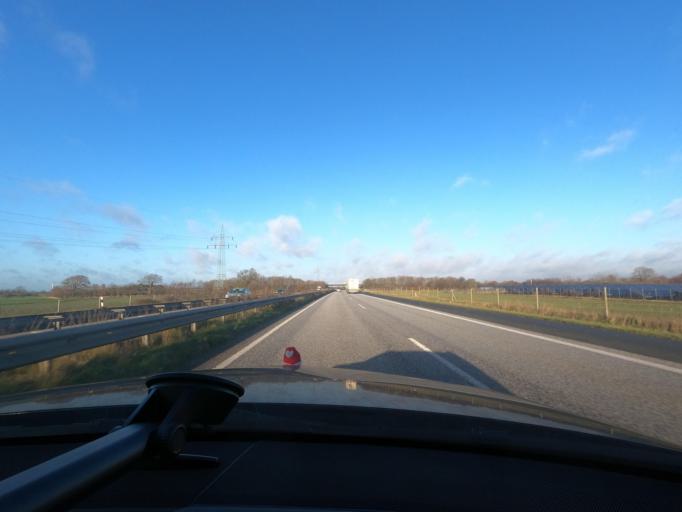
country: DE
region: Schleswig-Holstein
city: Lurschau
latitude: 54.5507
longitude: 9.4674
